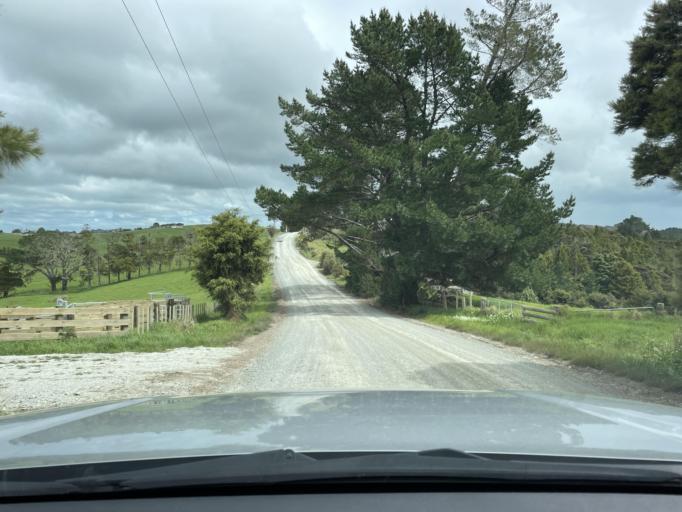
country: NZ
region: Auckland
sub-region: Auckland
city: Wellsford
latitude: -36.1709
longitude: 174.5794
